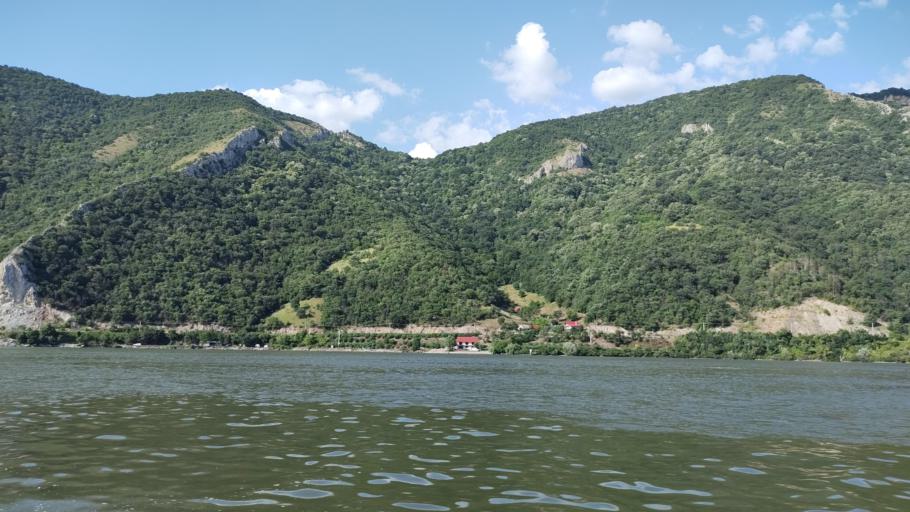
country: RO
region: Caras-Severin
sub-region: Comuna Berzasca
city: Berzasca
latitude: 44.5949
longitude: 22.0220
